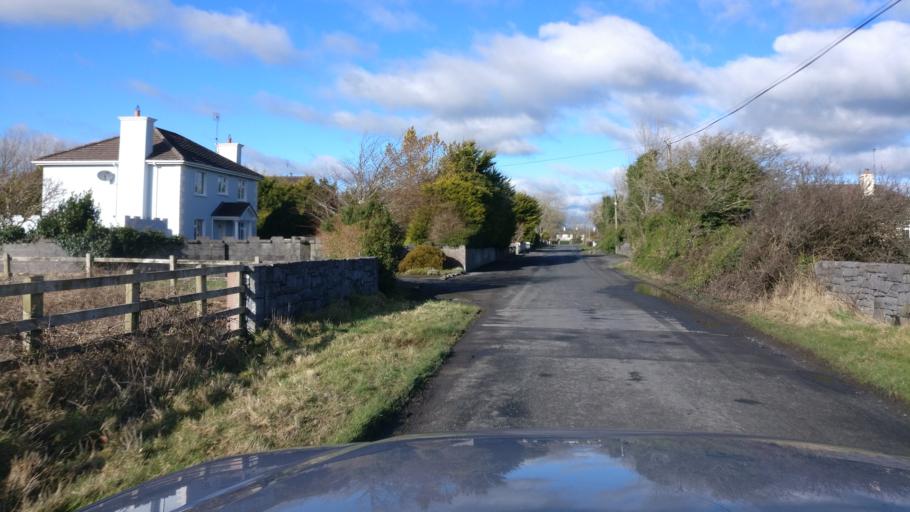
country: IE
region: Connaught
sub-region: County Galway
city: Oranmore
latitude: 53.2766
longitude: -8.9061
